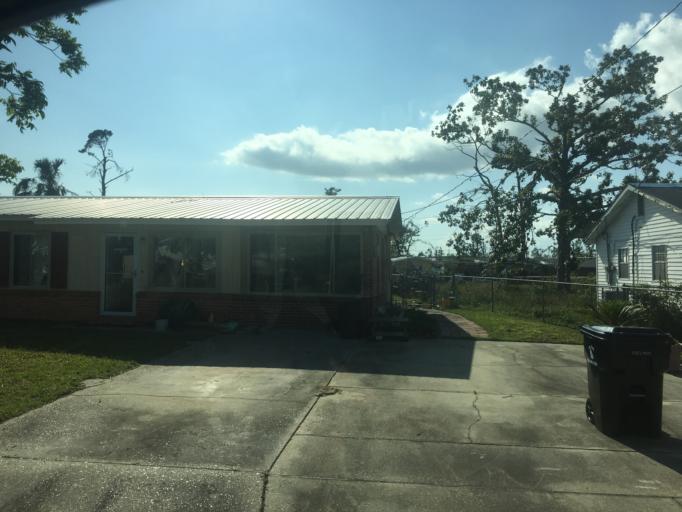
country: US
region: Florida
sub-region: Bay County
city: Cedar Grove
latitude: 30.1661
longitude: -85.6183
